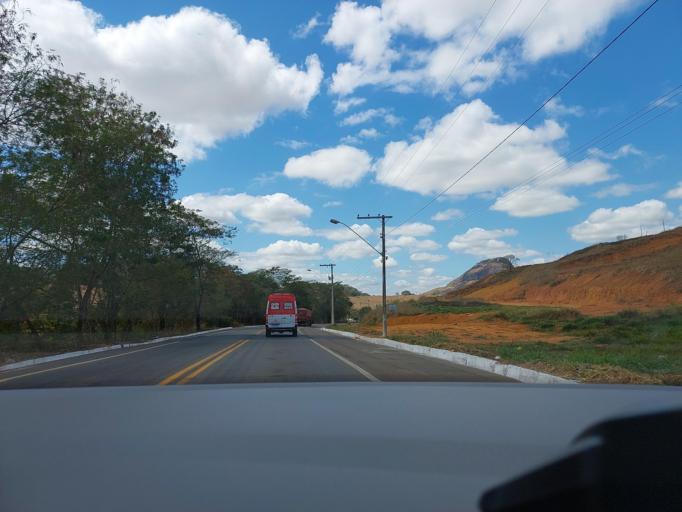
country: BR
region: Minas Gerais
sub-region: Muriae
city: Muriae
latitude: -21.1266
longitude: -42.3374
